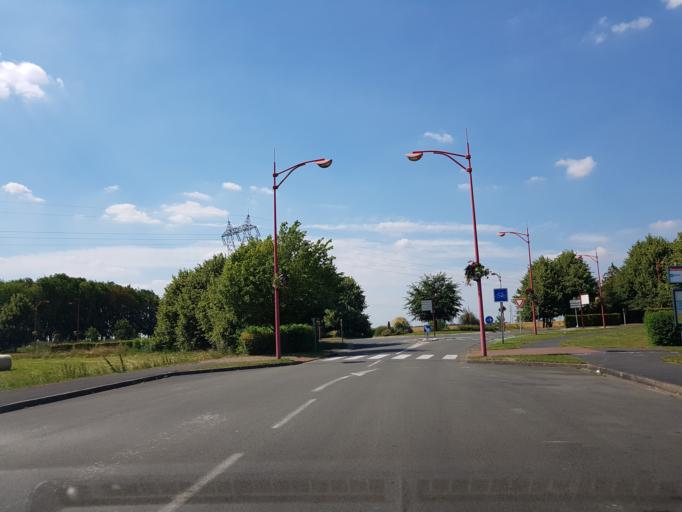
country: FR
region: Nord-Pas-de-Calais
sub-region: Departement du Nord
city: Roeulx
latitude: 50.3067
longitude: 3.3261
